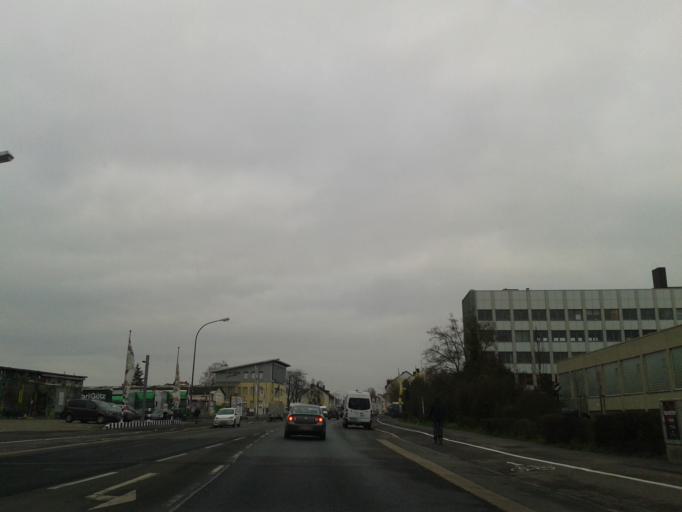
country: DE
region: Bavaria
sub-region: Upper Franconia
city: Hallstadt
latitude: 49.9132
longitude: 10.8788
